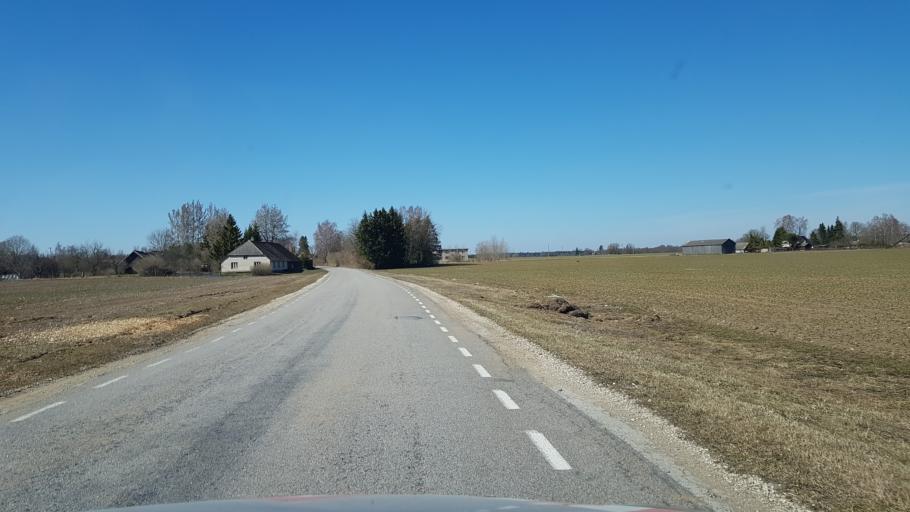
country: EE
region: Laeaene-Virumaa
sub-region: Vaeike-Maarja vald
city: Vaike-Maarja
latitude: 59.1102
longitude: 26.3761
